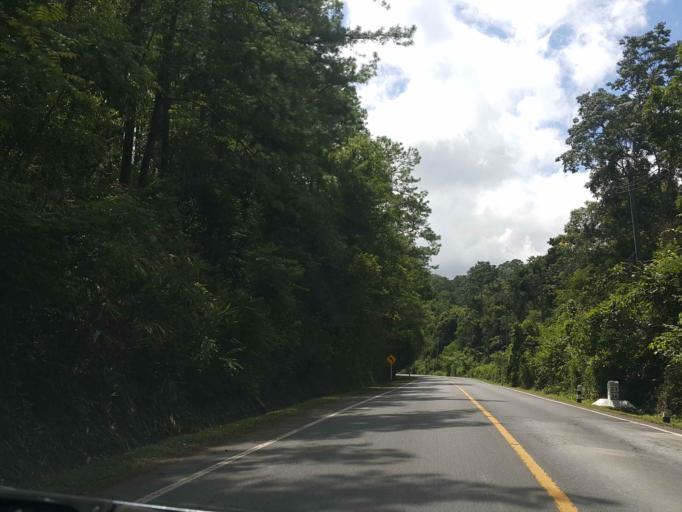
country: TH
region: Chiang Mai
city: Chom Thong
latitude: 18.5417
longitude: 98.5692
